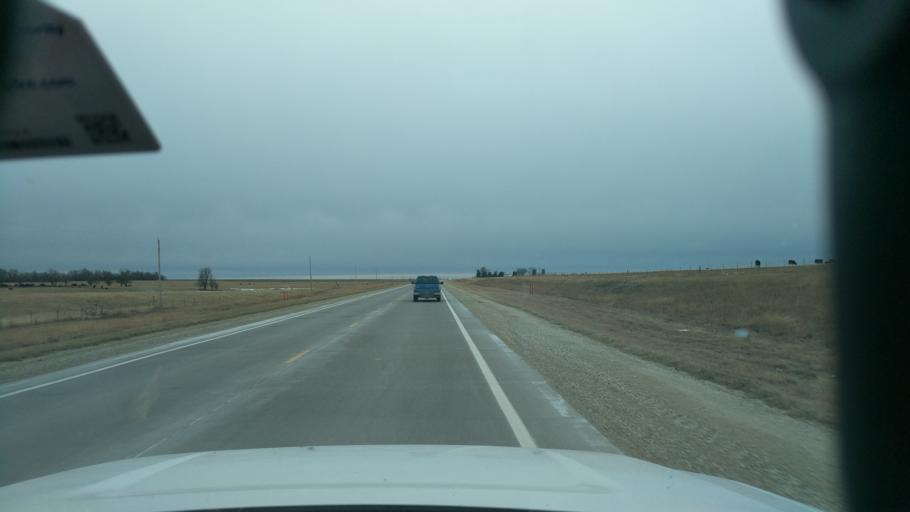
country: US
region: Kansas
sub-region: Dickinson County
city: Herington
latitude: 38.6055
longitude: -96.9486
